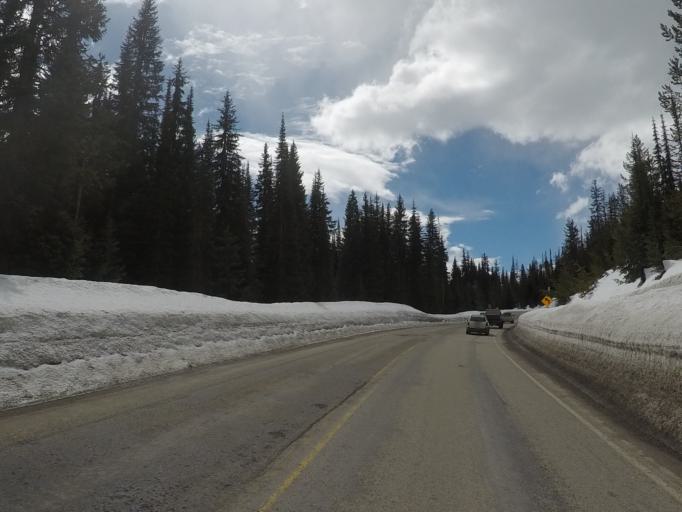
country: US
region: Montana
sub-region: Ravalli County
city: Stevensville
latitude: 46.6395
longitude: -114.5803
